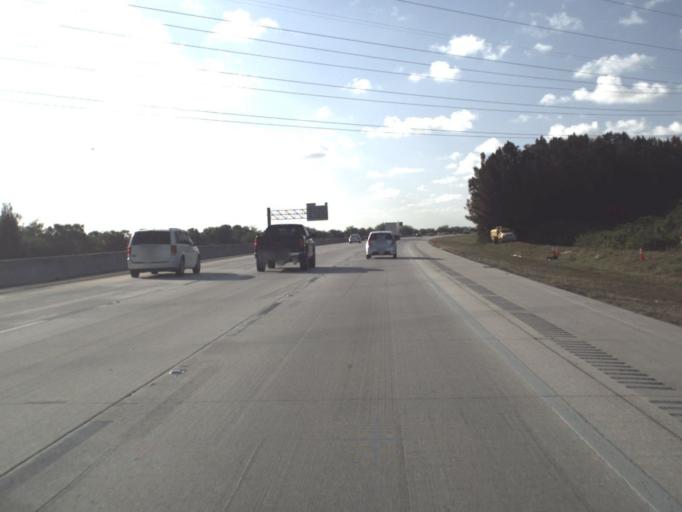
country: US
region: Florida
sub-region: Brevard County
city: Rockledge
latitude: 28.3000
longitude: -80.7538
